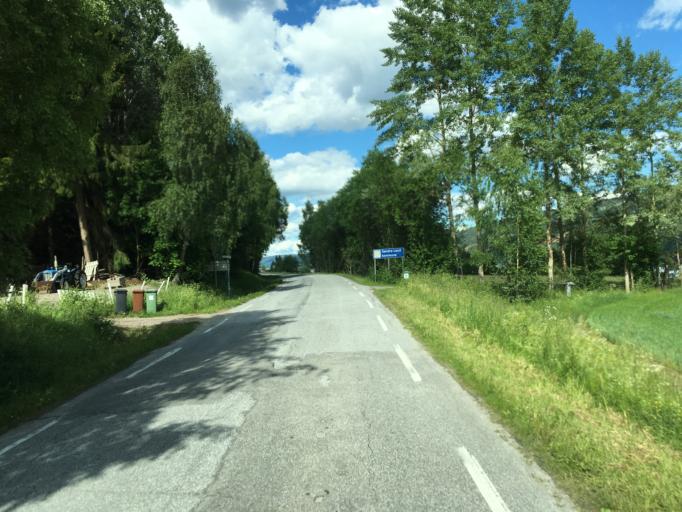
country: NO
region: Oppland
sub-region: Sondre Land
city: Hov
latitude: 60.5273
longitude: 10.2883
